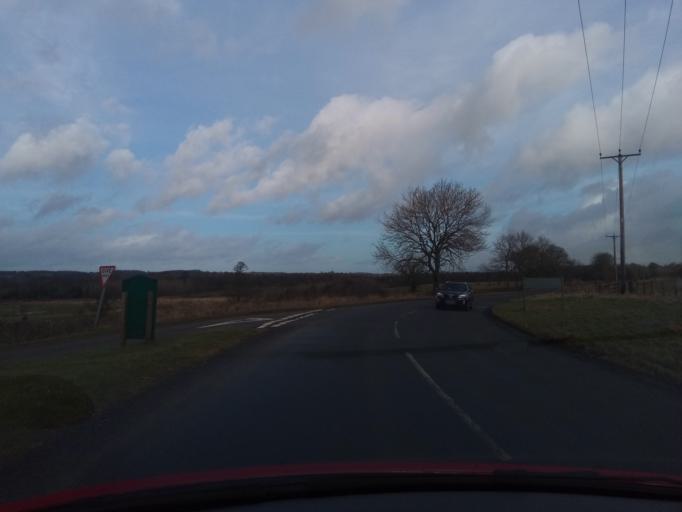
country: GB
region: England
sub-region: Northumberland
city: Rothley
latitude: 55.1343
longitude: -1.9790
